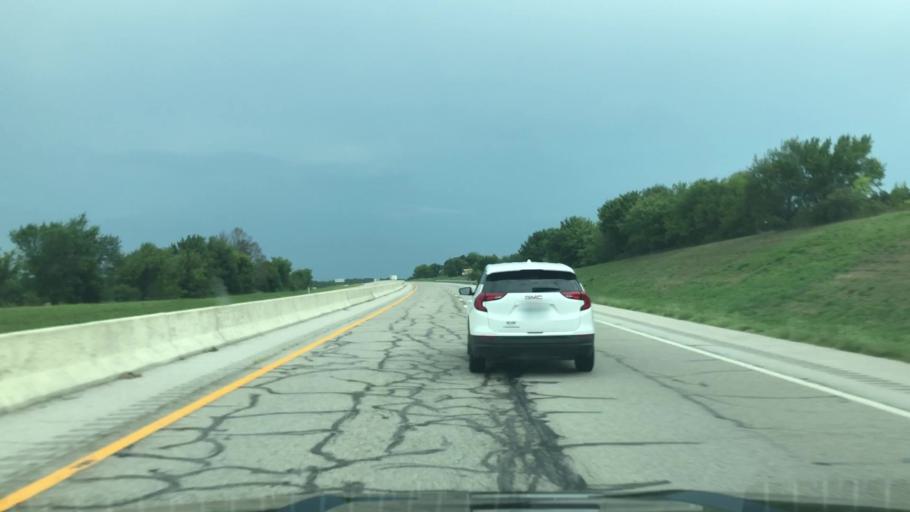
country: US
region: Oklahoma
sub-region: Rogers County
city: Chelsea
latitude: 36.4480
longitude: -95.3705
